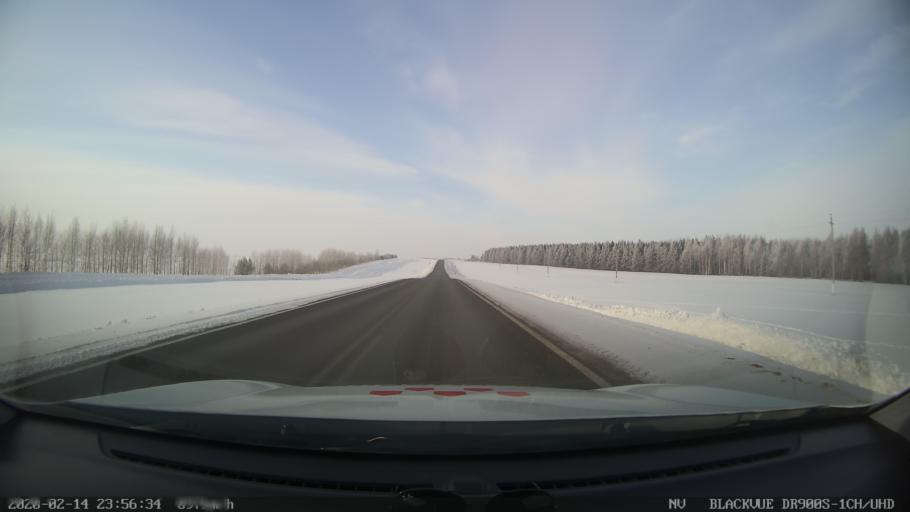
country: RU
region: Tatarstan
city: Kuybyshevskiy Zaton
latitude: 55.3260
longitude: 49.1278
